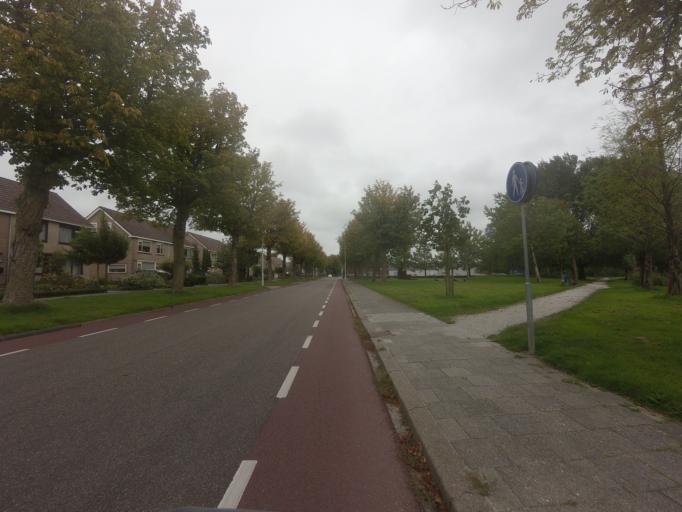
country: NL
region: Friesland
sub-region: Gemeente Leeuwarderadeel
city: Stiens
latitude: 53.2576
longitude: 5.7632
